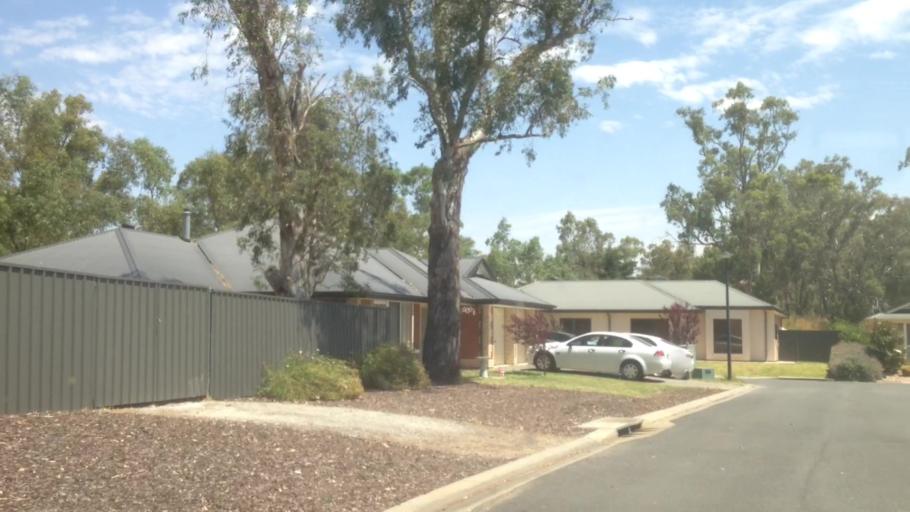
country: AU
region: South Australia
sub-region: Adelaide Hills
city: Birdwood
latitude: -34.8175
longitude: 138.9705
